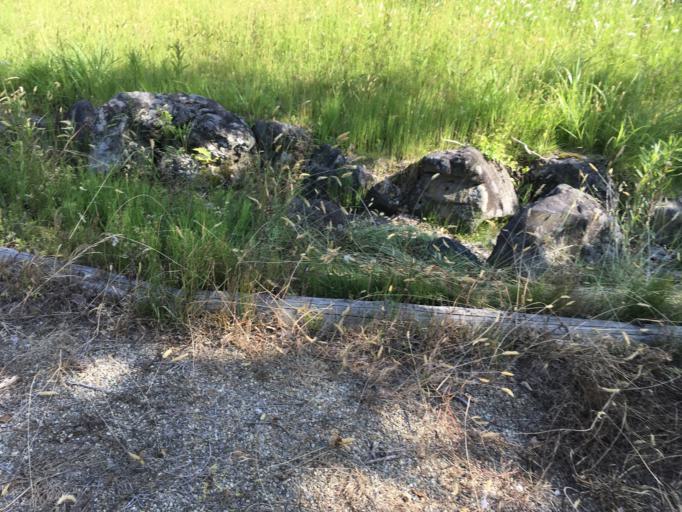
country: JP
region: Miyagi
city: Wakuya
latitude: 38.6688
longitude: 141.1392
